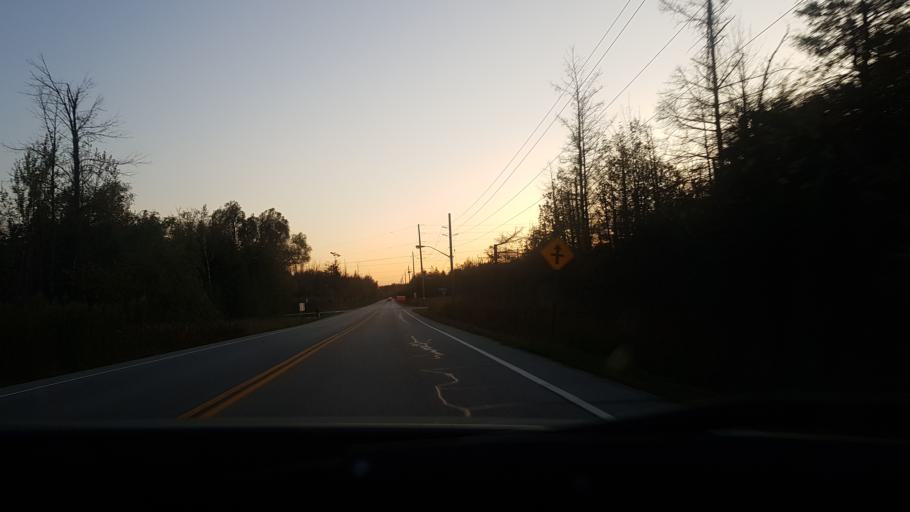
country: CA
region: Ontario
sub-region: Halton
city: Milton
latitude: 43.4768
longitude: -79.9915
